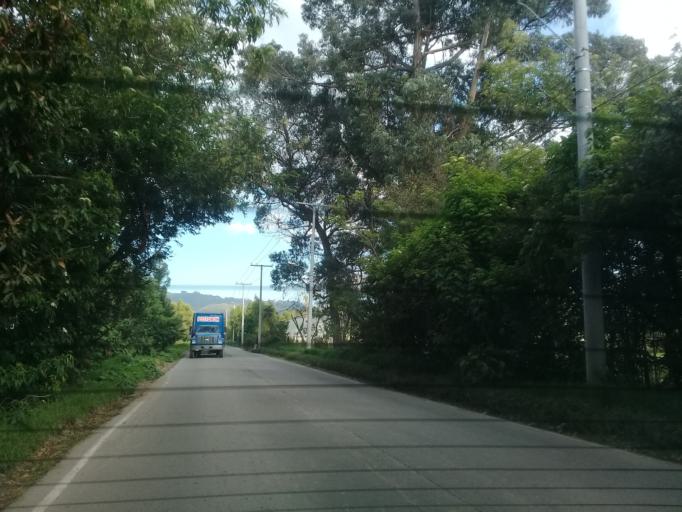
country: CO
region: Cundinamarca
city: El Rosal
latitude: 4.8188
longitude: -74.2329
